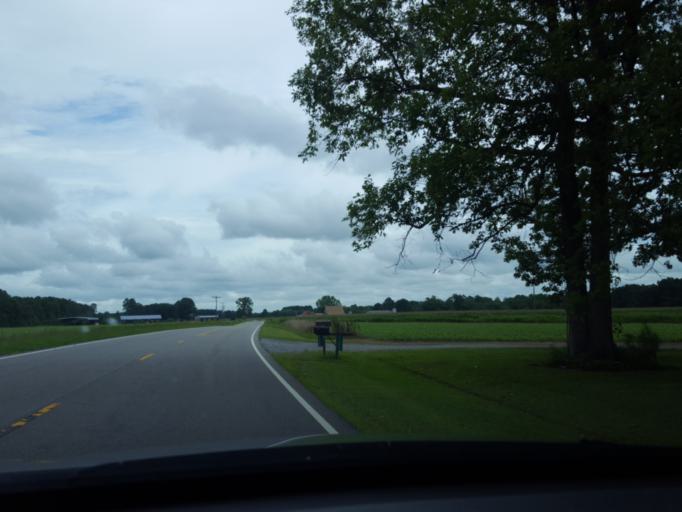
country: US
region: North Carolina
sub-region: Beaufort County
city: Washington
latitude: 35.6975
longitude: -76.9888
